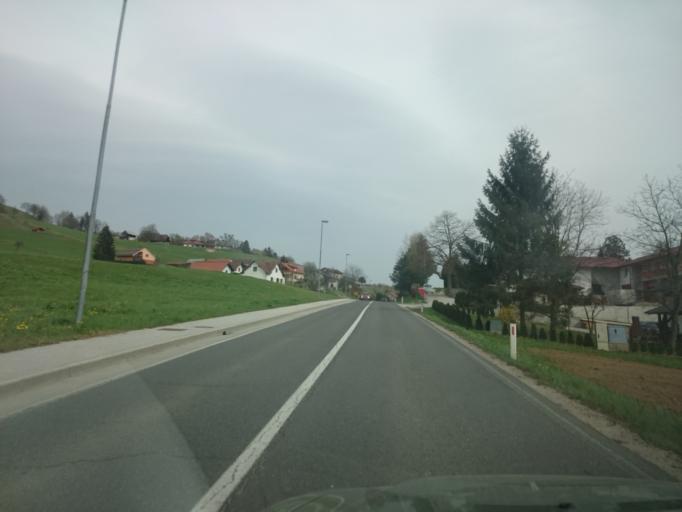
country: SI
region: Store
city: Store
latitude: 46.2191
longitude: 15.3526
